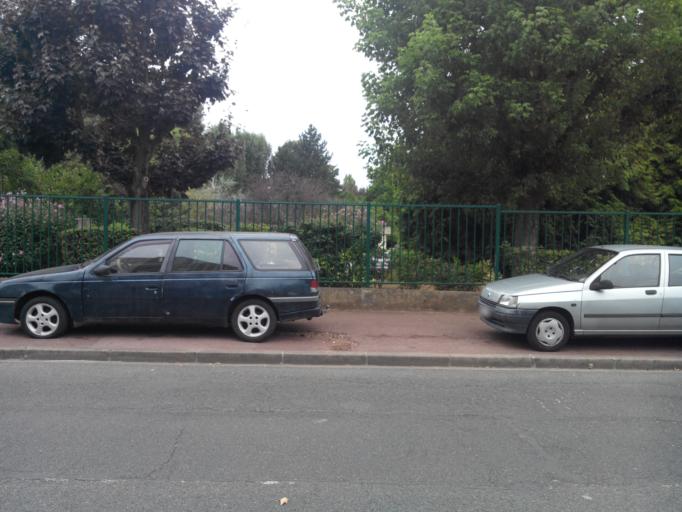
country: FR
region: Ile-de-France
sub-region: Departement du Val-de-Marne
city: L'Hay-les-Roses
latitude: 48.7880
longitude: 2.3326
